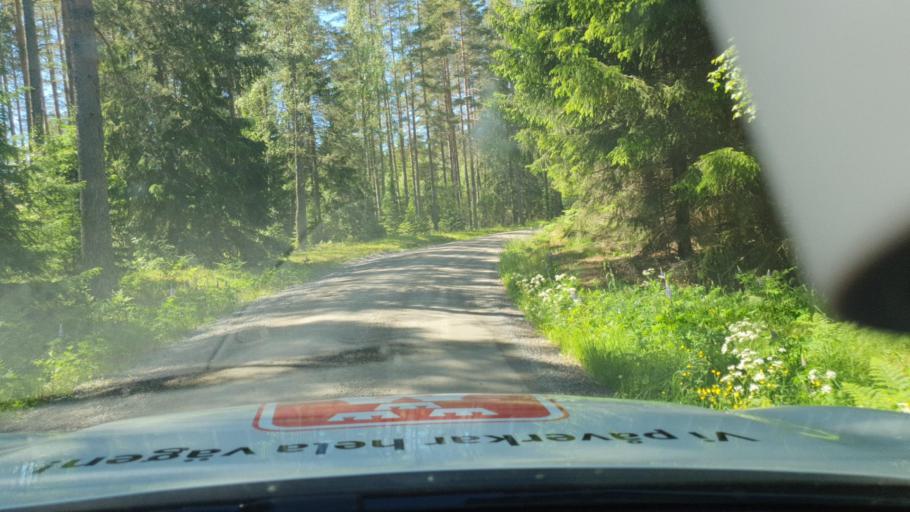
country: SE
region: Joenkoeping
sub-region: Mullsjo Kommun
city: Mullsjoe
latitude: 57.8901
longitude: 13.9651
